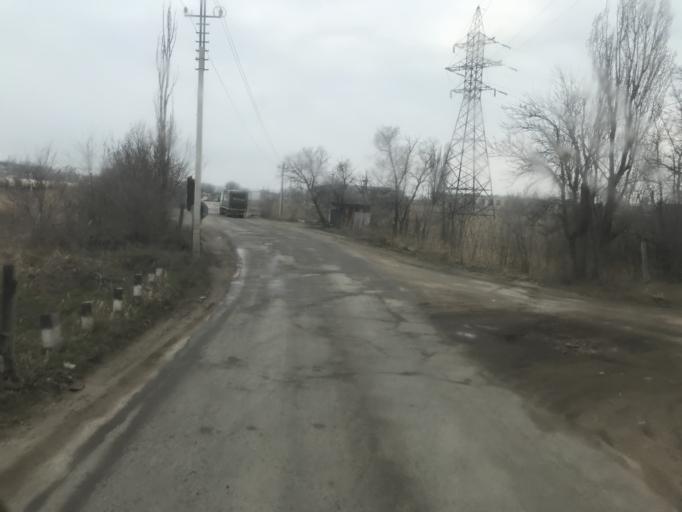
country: RU
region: Volgograd
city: Krasnoslobodsk
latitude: 48.5290
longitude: 44.5922
